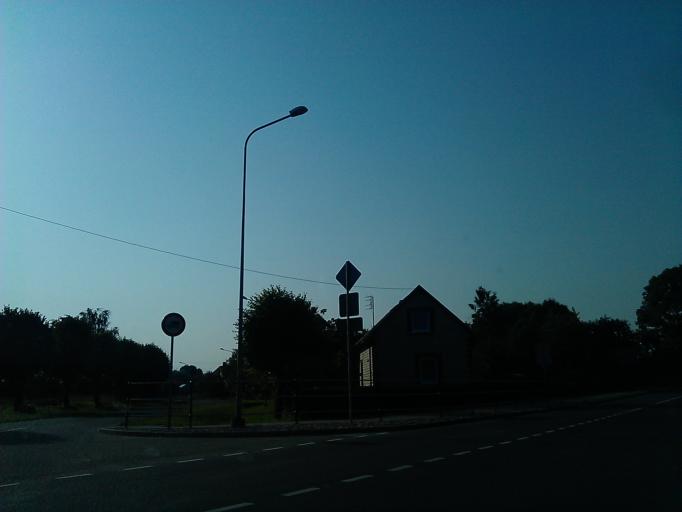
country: LV
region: Aizpute
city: Aizpute
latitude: 56.7155
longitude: 21.6156
